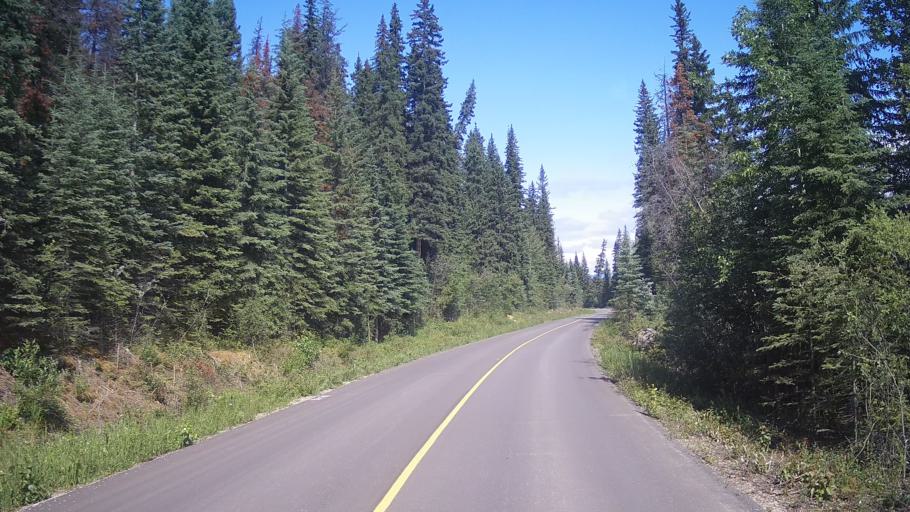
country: CA
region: Alberta
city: Jasper Park Lodge
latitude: 52.7366
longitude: -117.9570
